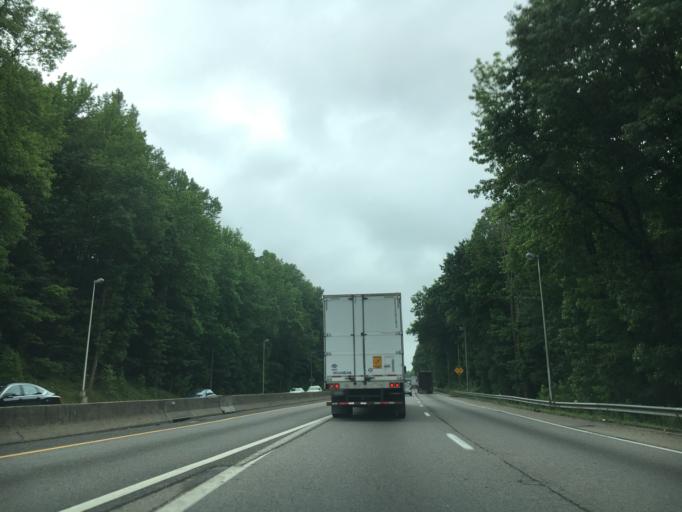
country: US
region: Virginia
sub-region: City of Petersburg
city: Petersburg
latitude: 37.2169
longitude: -77.3927
